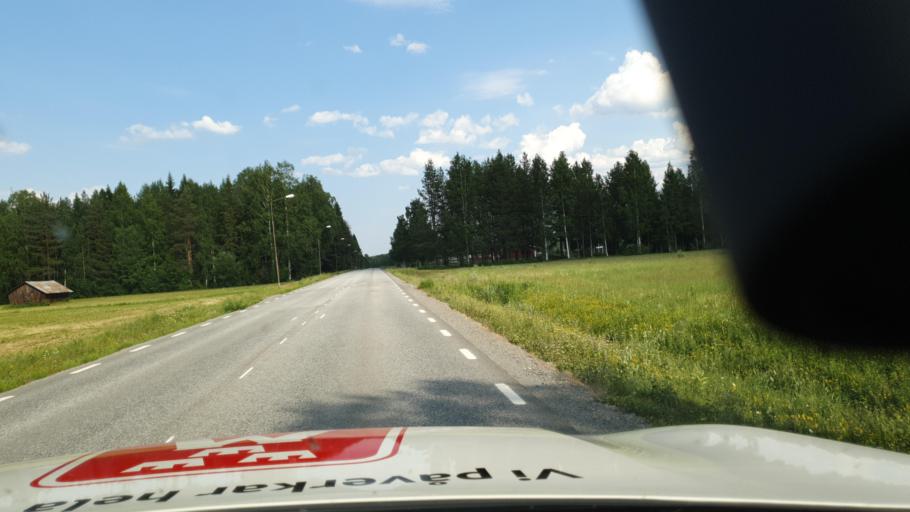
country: SE
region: Vaesterbotten
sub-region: Skelleftea Kommun
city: Viken
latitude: 64.7412
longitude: 20.8058
